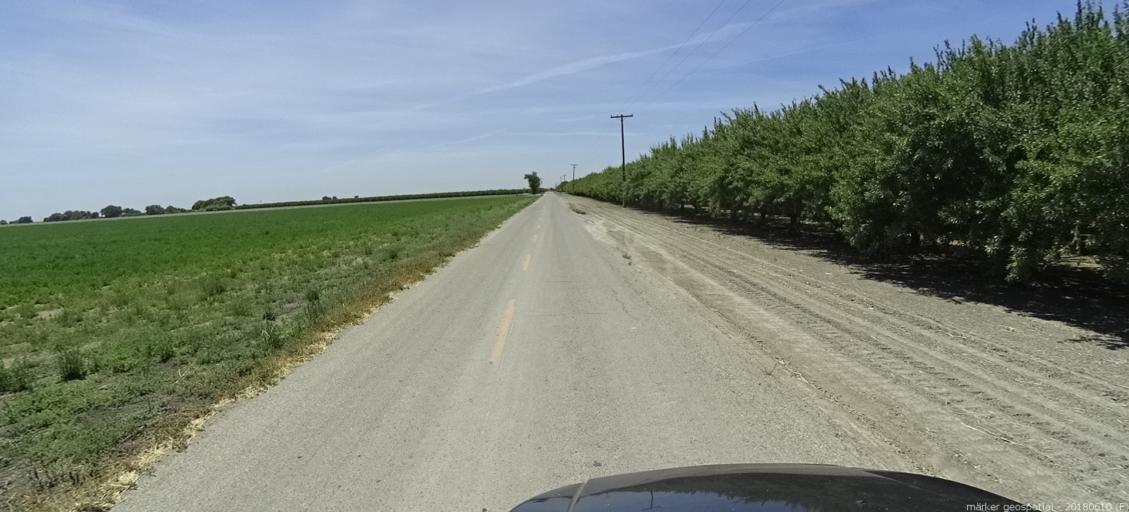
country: US
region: California
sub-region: Merced County
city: Dos Palos
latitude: 37.0281
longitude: -120.5288
